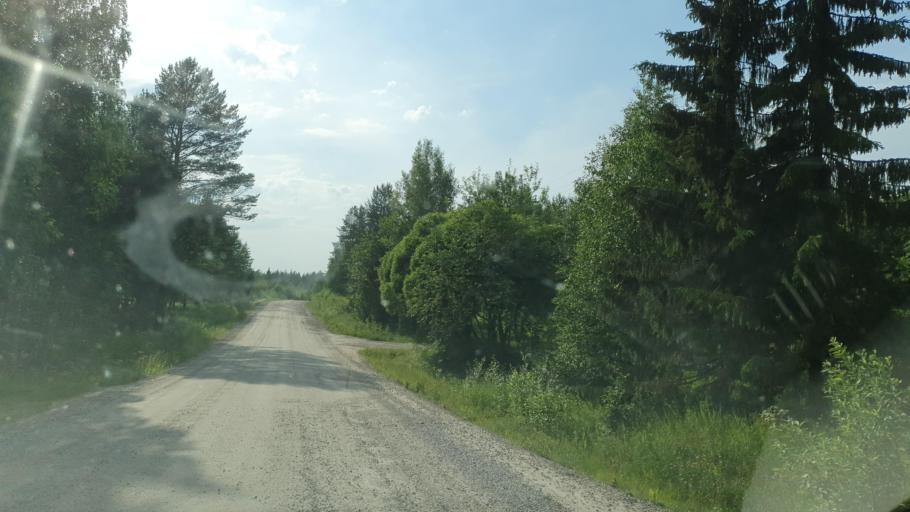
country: FI
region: Kainuu
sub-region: Kehys-Kainuu
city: Kuhmo
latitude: 64.1024
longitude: 29.5442
